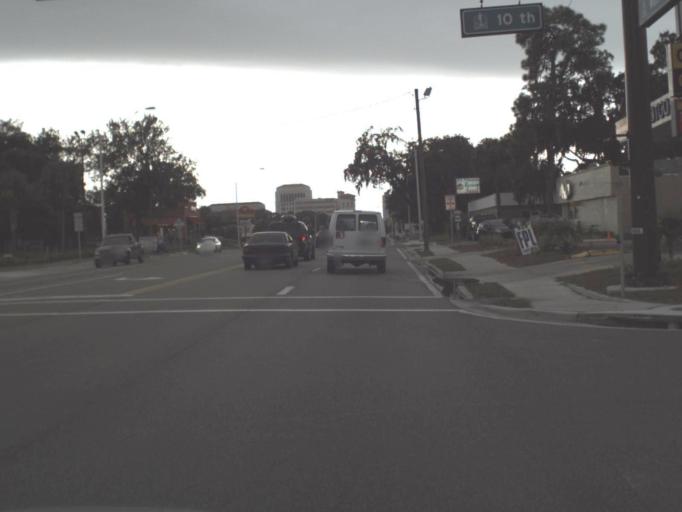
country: US
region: Florida
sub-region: Sarasota County
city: Sarasota
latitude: 27.3446
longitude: -82.5311
